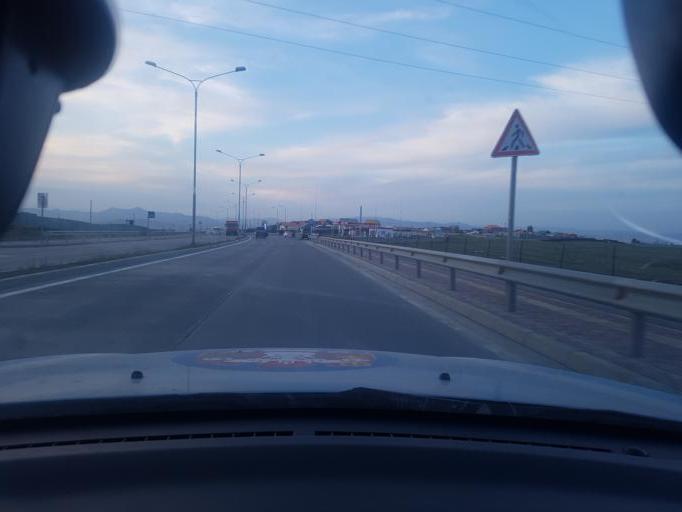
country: MN
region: Ulaanbaatar
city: Ulaanbaatar
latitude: 47.8612
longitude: 106.7879
